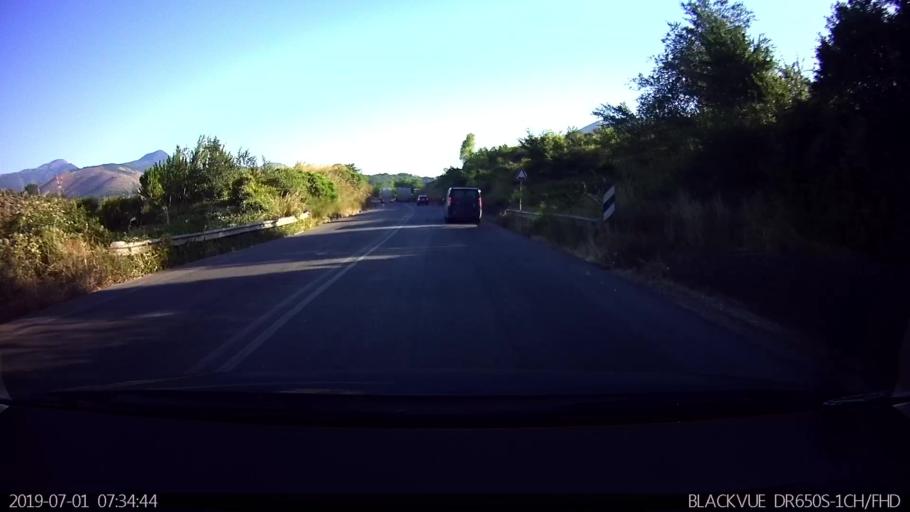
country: IT
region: Latium
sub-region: Provincia di Latina
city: Prossedi
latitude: 41.5185
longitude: 13.2729
